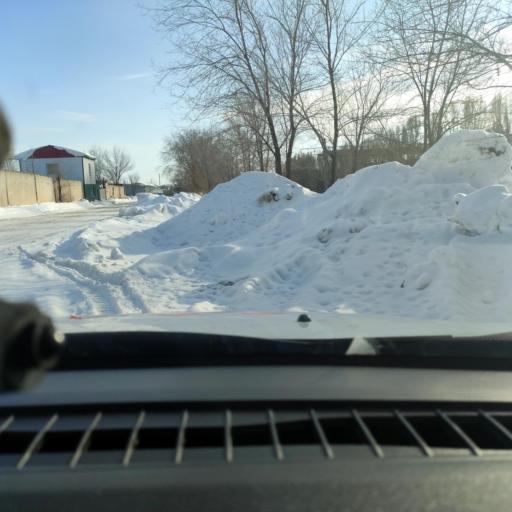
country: RU
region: Samara
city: Petra-Dubrava
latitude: 53.2617
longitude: 50.3549
